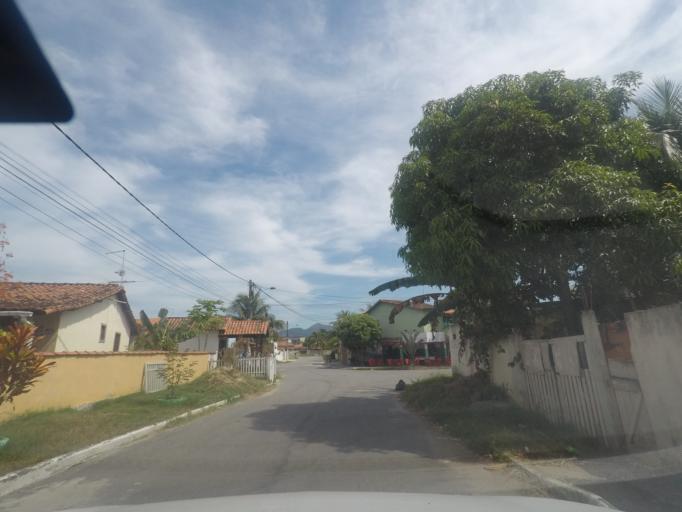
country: BR
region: Rio de Janeiro
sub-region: Marica
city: Marica
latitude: -22.9519
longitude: -42.7500
